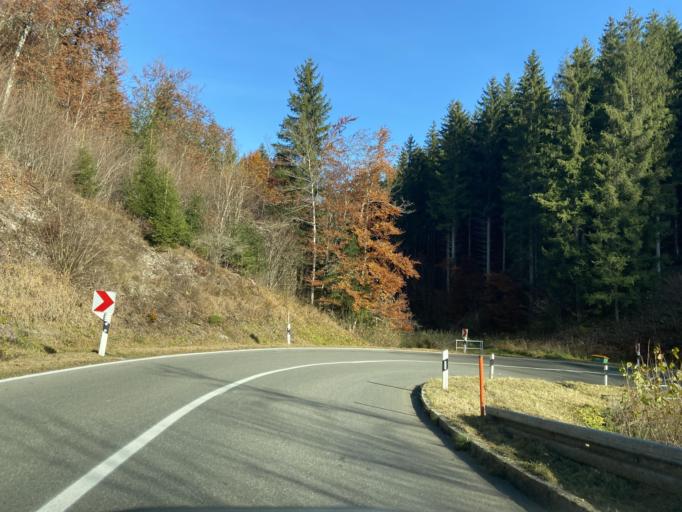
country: DE
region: Baden-Wuerttemberg
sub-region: Tuebingen Region
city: Stetten am Kalten Markt
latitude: 48.1054
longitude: 9.0937
